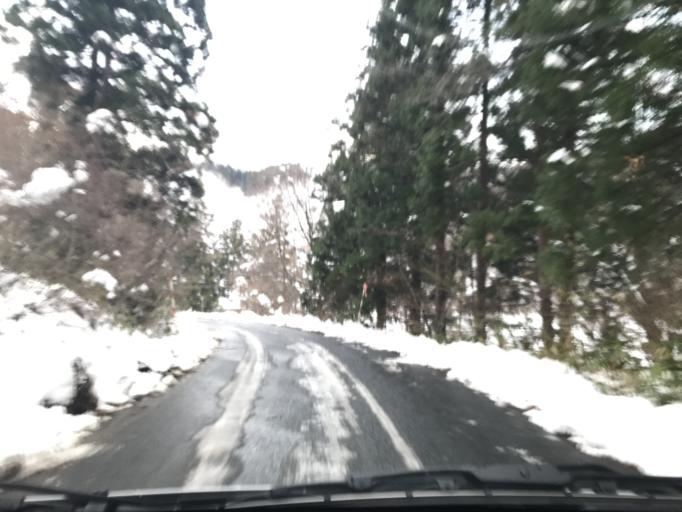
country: JP
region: Iwate
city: Mizusawa
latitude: 39.0457
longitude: 141.0194
